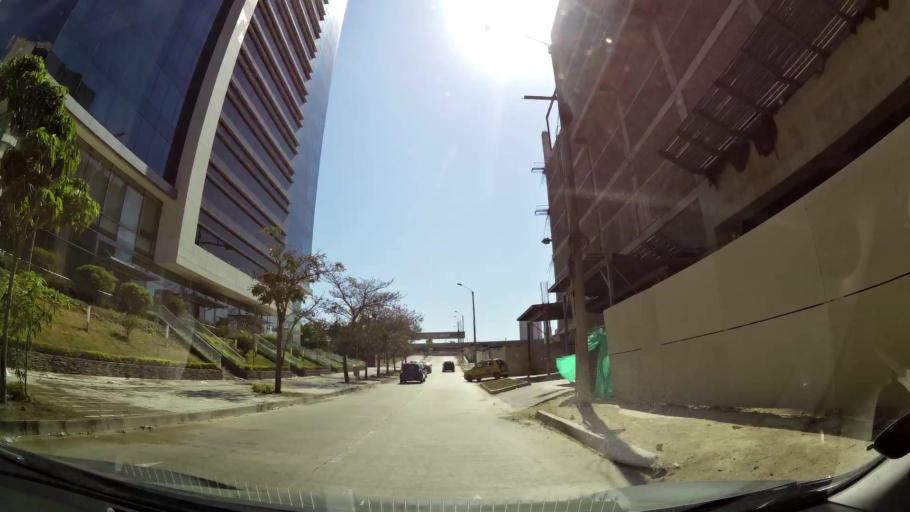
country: CO
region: Atlantico
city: Barranquilla
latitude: 11.0161
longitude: -74.8284
